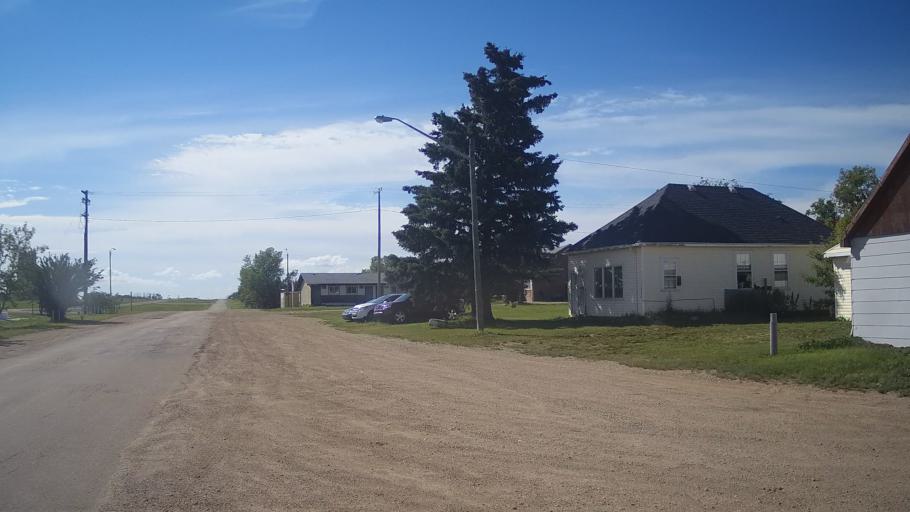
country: CA
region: Saskatchewan
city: Foam Lake
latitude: 51.2622
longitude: -103.7369
